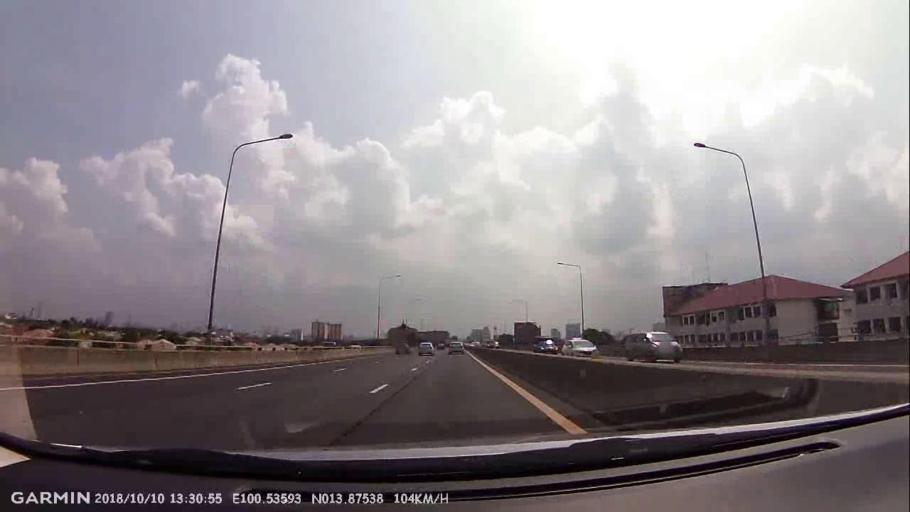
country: TH
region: Nonthaburi
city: Mueang Nonthaburi
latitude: 13.8752
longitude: 100.5359
